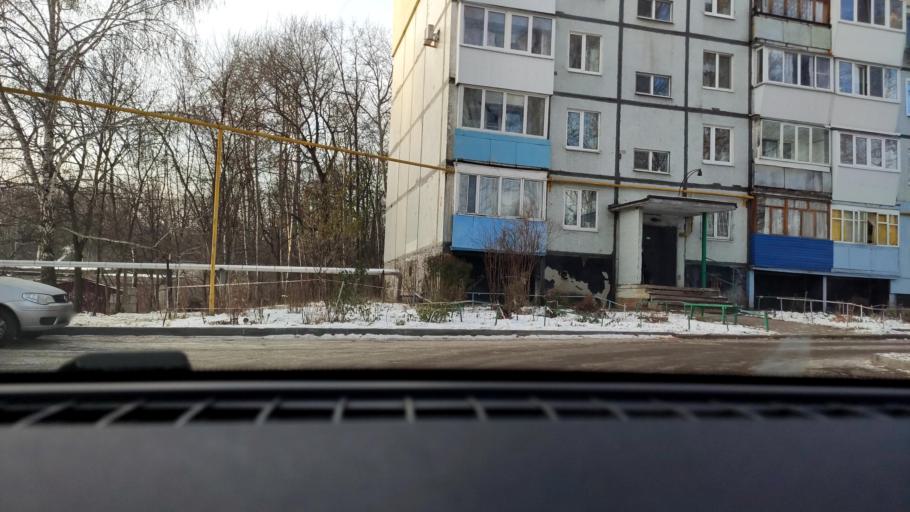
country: RU
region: Samara
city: Petra-Dubrava
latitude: 53.3025
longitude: 50.2680
